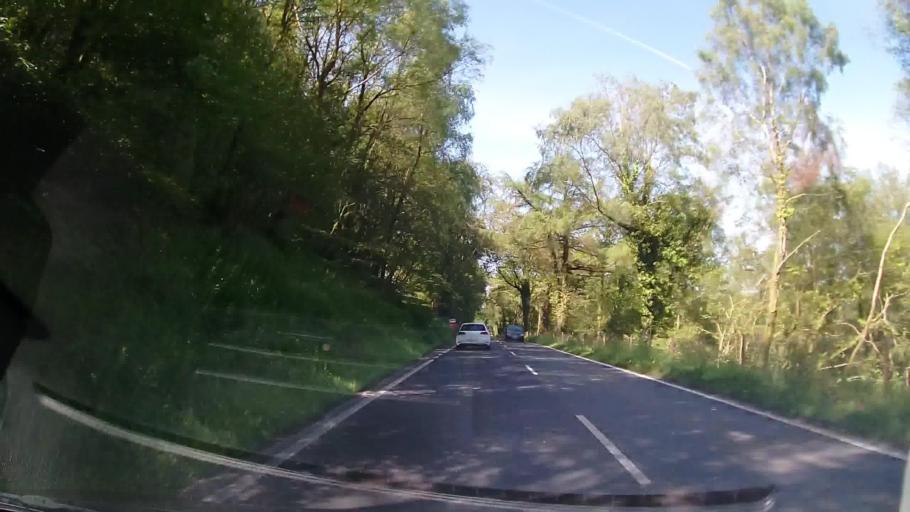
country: GB
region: Wales
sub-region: Gwynedd
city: Corris
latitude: 52.6154
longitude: -3.7750
